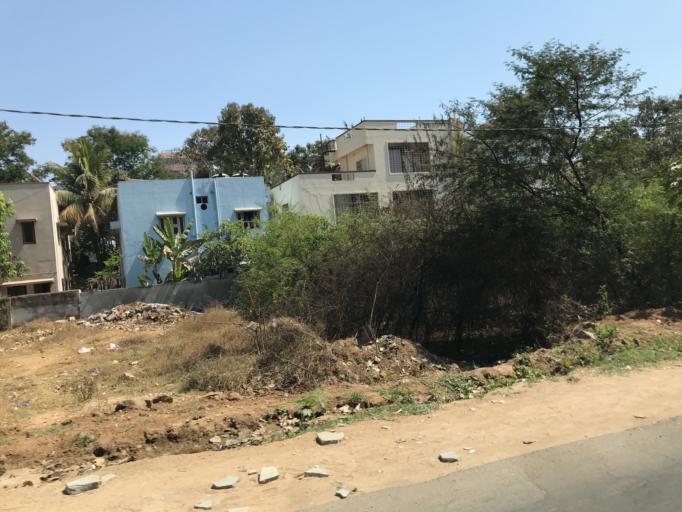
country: IN
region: Telangana
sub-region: Medak
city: Serilingampalle
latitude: 17.4745
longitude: 78.3263
